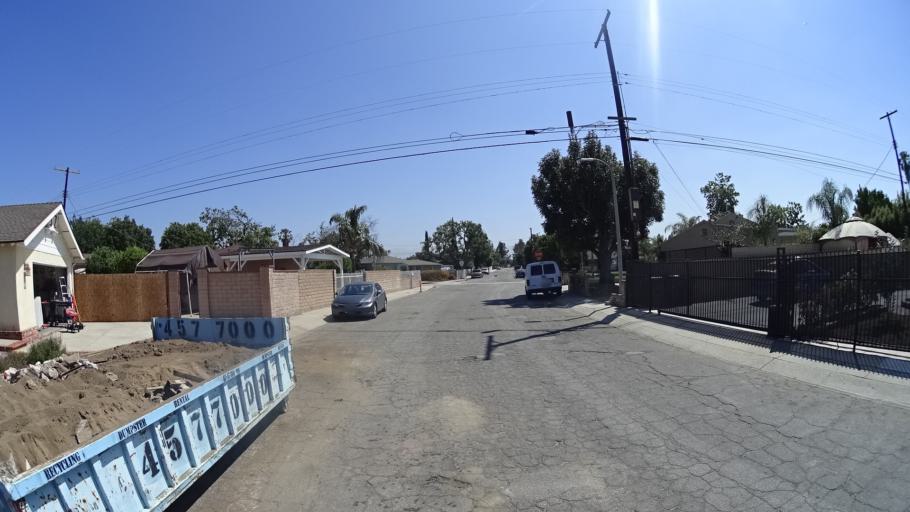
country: US
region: California
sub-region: Los Angeles County
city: Van Nuys
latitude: 34.2261
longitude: -118.4457
